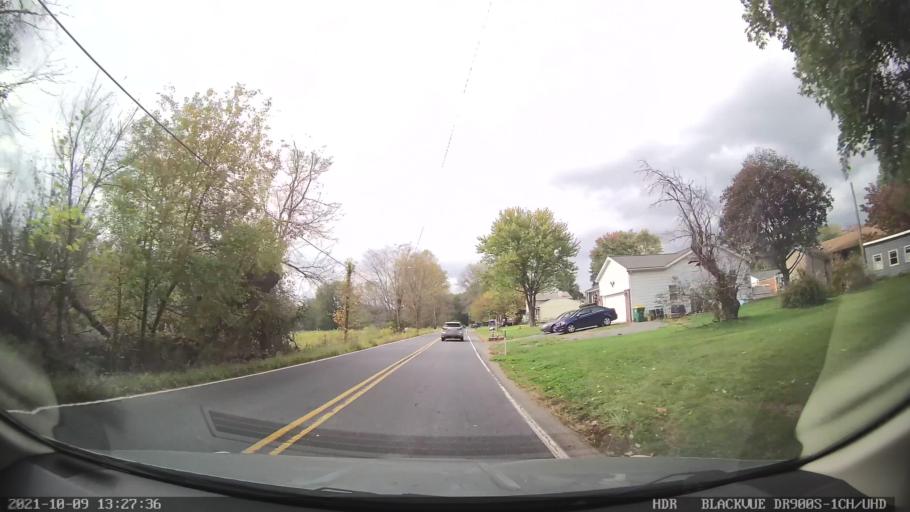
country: US
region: Pennsylvania
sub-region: Lehigh County
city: Ancient Oaks
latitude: 40.5423
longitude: -75.5850
